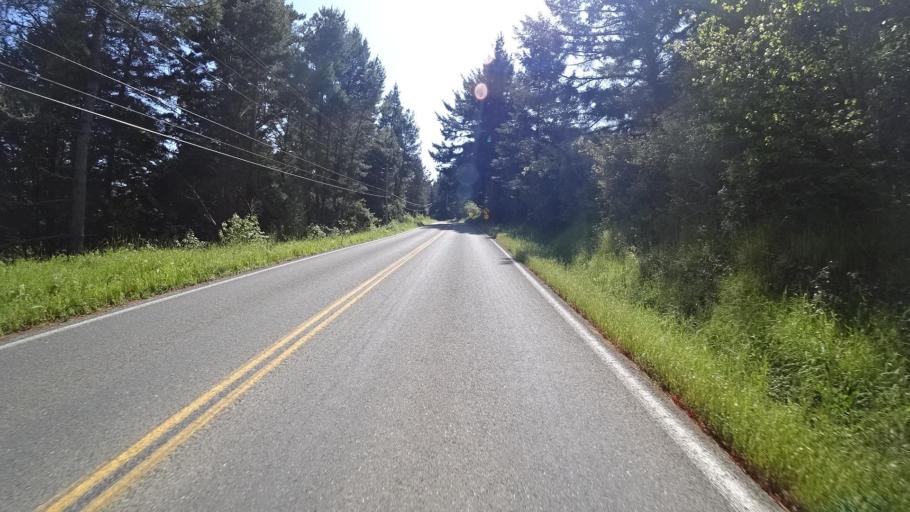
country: US
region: California
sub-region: Humboldt County
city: Hydesville
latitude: 40.5538
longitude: -124.1102
